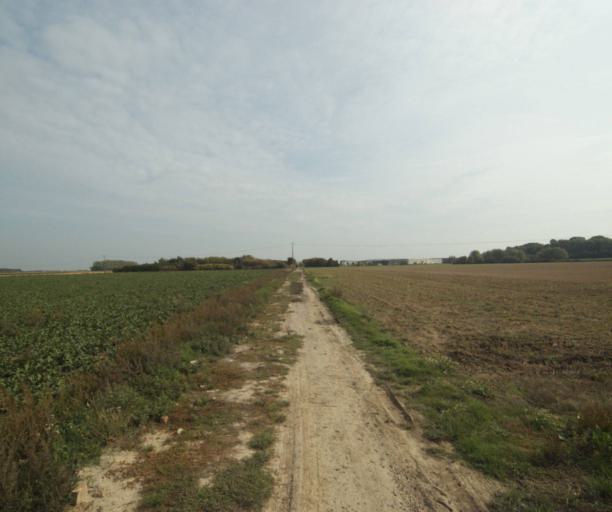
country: FR
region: Nord-Pas-de-Calais
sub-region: Departement du Nord
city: Templemars
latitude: 50.5605
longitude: 3.0517
